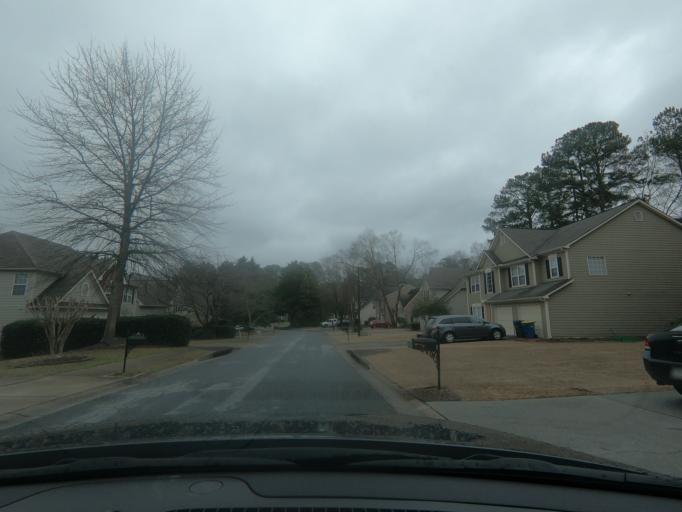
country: US
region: Georgia
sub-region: Cobb County
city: Kennesaw
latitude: 34.0492
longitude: -84.6401
